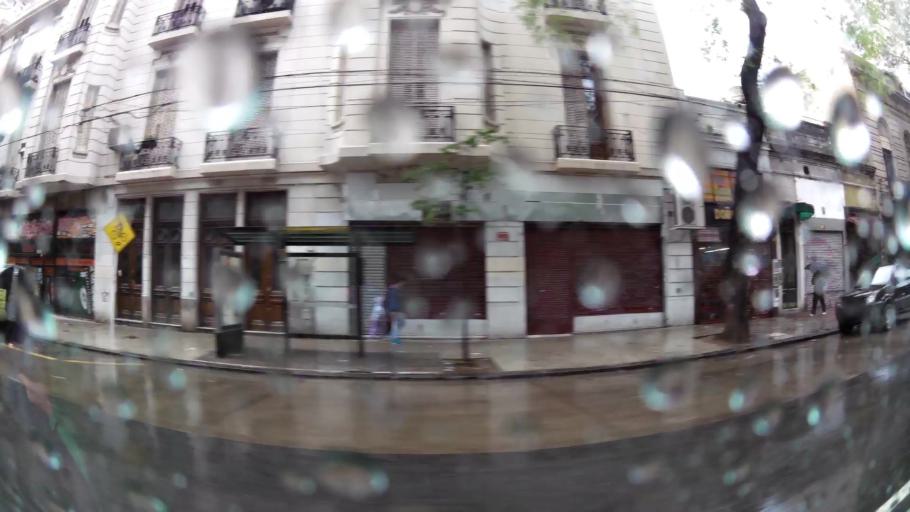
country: AR
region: Buenos Aires F.D.
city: Buenos Aires
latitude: -34.6206
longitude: -58.3915
